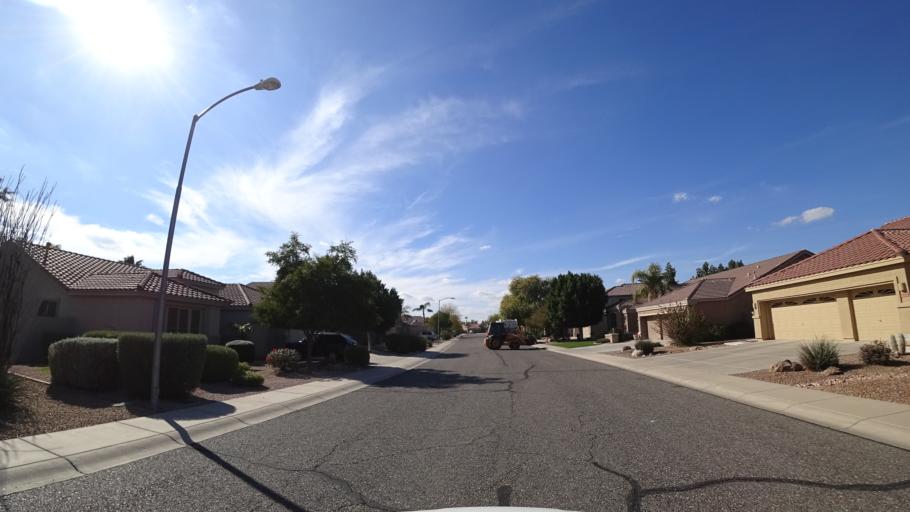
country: US
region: Arizona
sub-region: Maricopa County
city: Sun City
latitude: 33.6803
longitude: -112.2139
